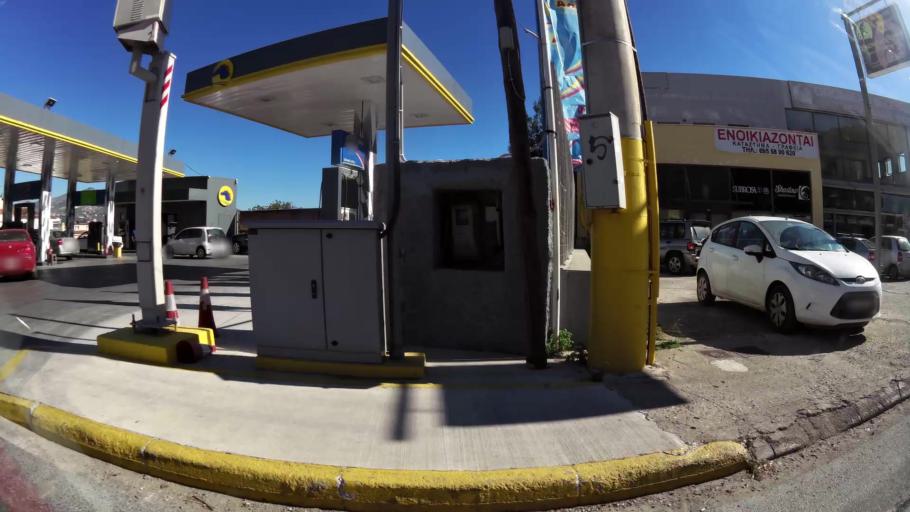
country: GR
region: Attica
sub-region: Nomarchia Athinas
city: Agia Paraskevi
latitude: 38.0055
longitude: 23.8468
